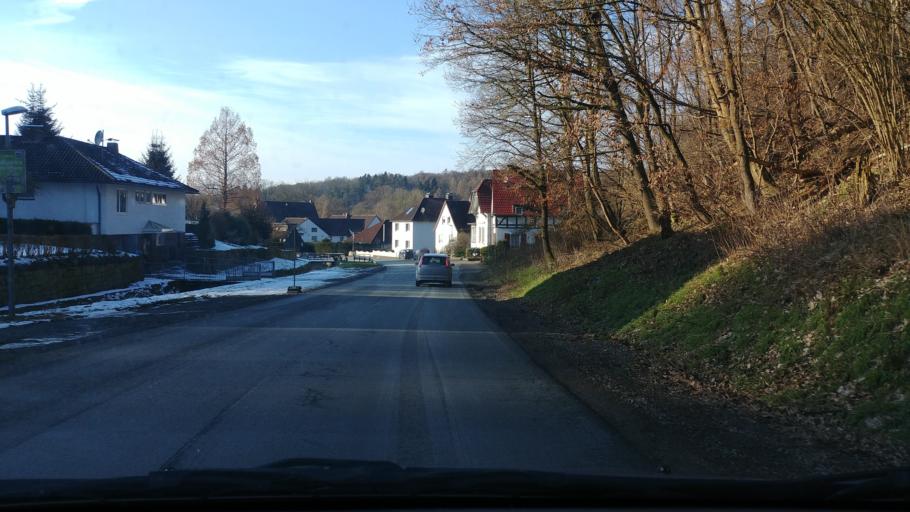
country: DE
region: Hesse
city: Trendelburg
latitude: 51.5750
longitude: 9.4336
